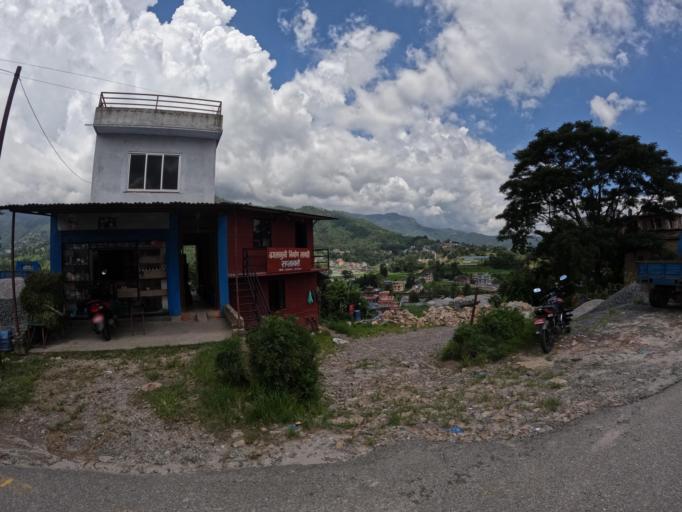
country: NP
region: Central Region
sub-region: Bagmati Zone
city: Kathmandu
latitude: 27.7757
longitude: 85.3278
